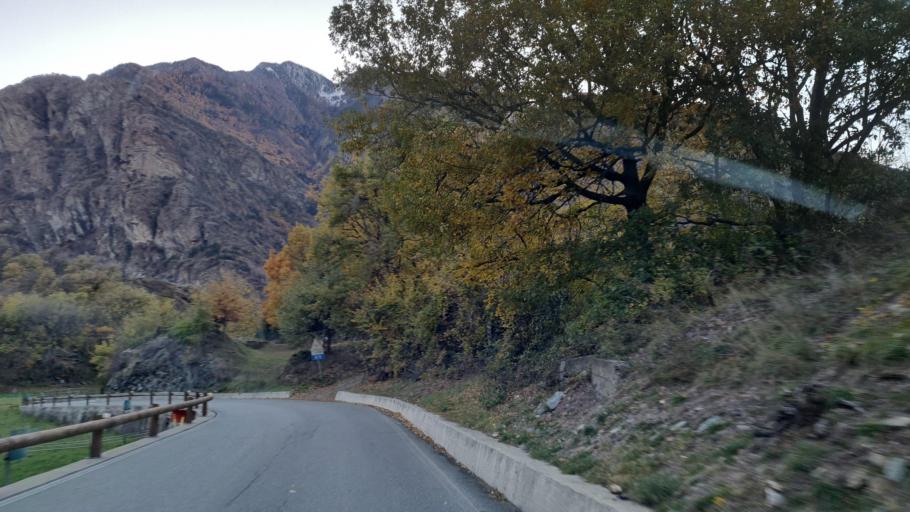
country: IT
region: Aosta Valley
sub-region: Valle d'Aosta
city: Emarese
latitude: 45.7283
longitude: 7.6704
